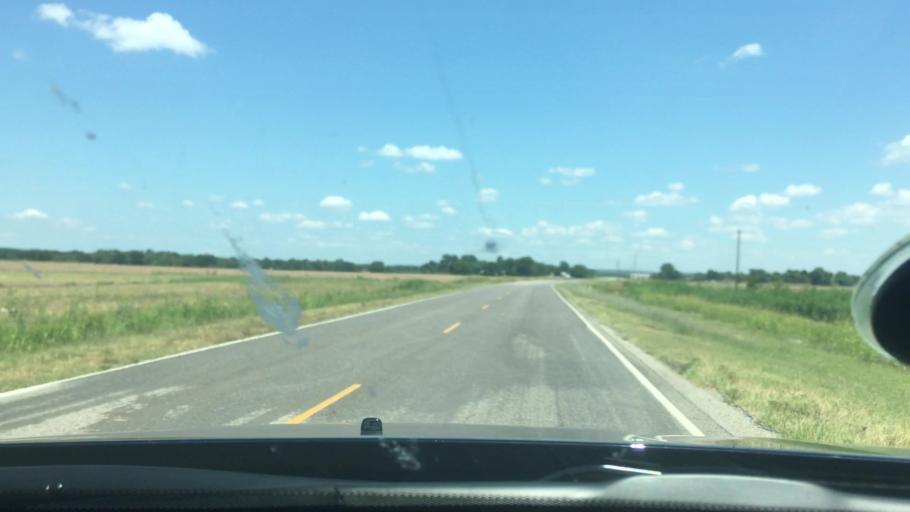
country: US
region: Oklahoma
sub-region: Carter County
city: Dickson
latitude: 34.2240
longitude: -96.9771
